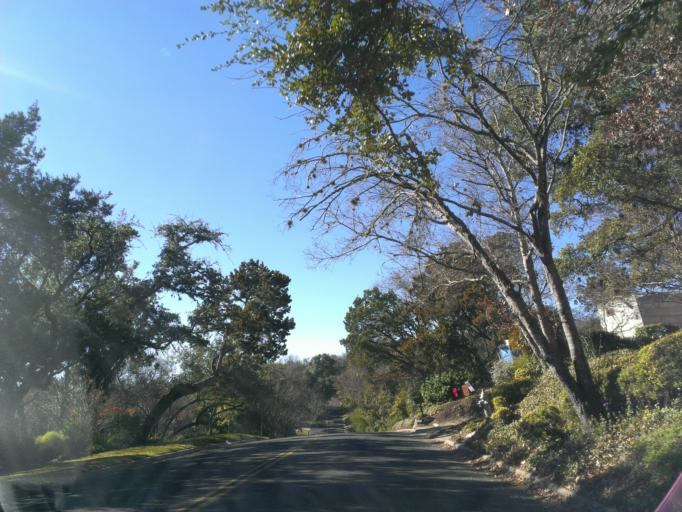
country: US
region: Texas
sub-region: Travis County
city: West Lake Hills
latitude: 30.3267
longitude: -97.7670
